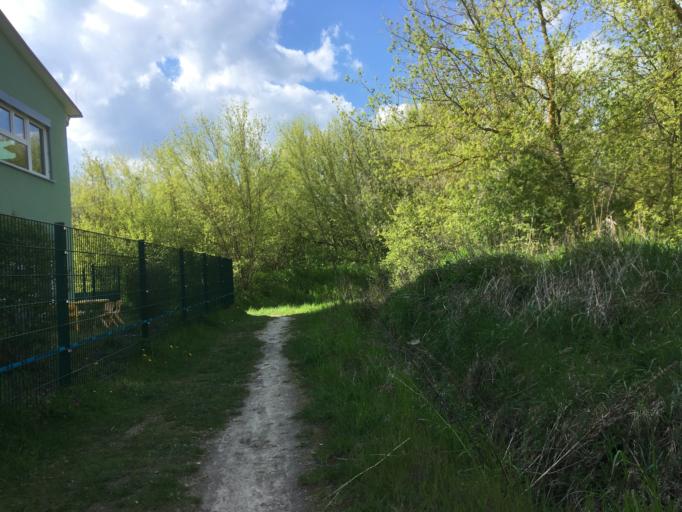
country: DE
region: Berlin
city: Hellersdorf
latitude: 52.5374
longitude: 13.6285
